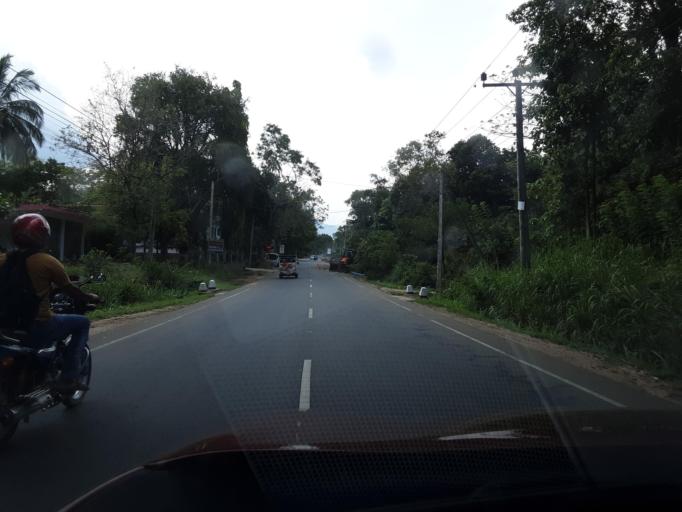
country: LK
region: Uva
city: Haputale
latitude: 6.6823
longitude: 81.1095
